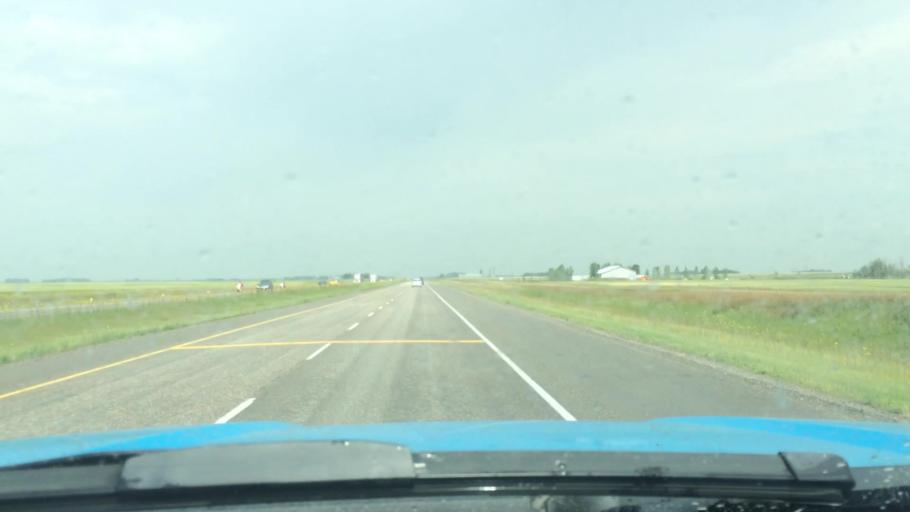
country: CA
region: Alberta
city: Didsbury
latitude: 51.6960
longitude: -114.0253
